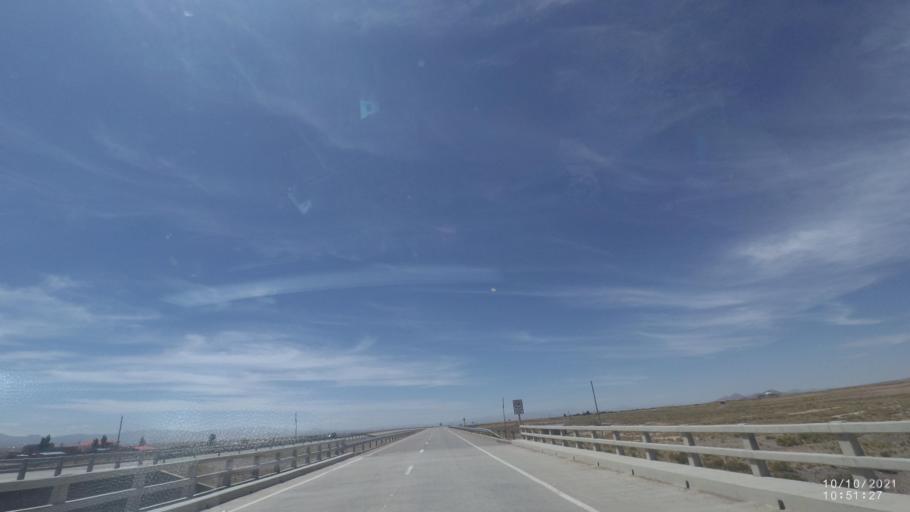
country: BO
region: La Paz
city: Colquiri
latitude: -17.6529
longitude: -67.2128
